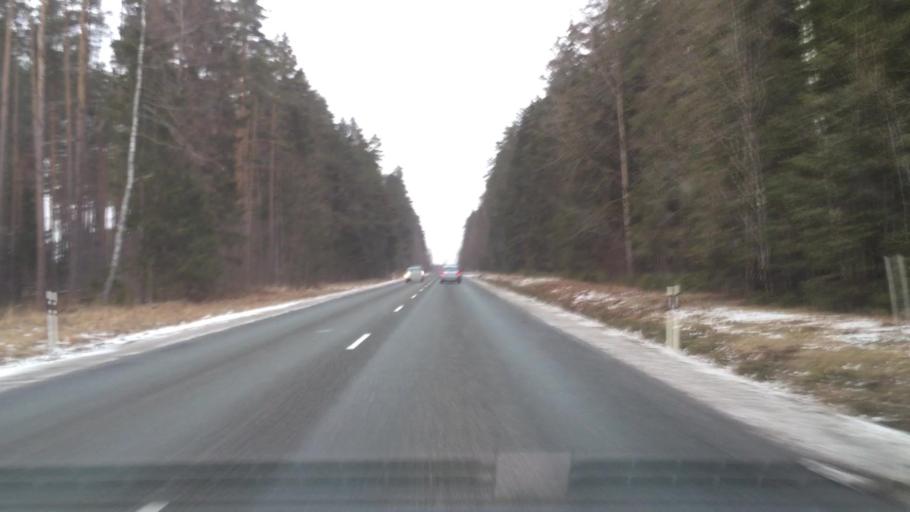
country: LV
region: Valmieras Rajons
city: Valmiera
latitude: 57.5025
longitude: 25.4193
